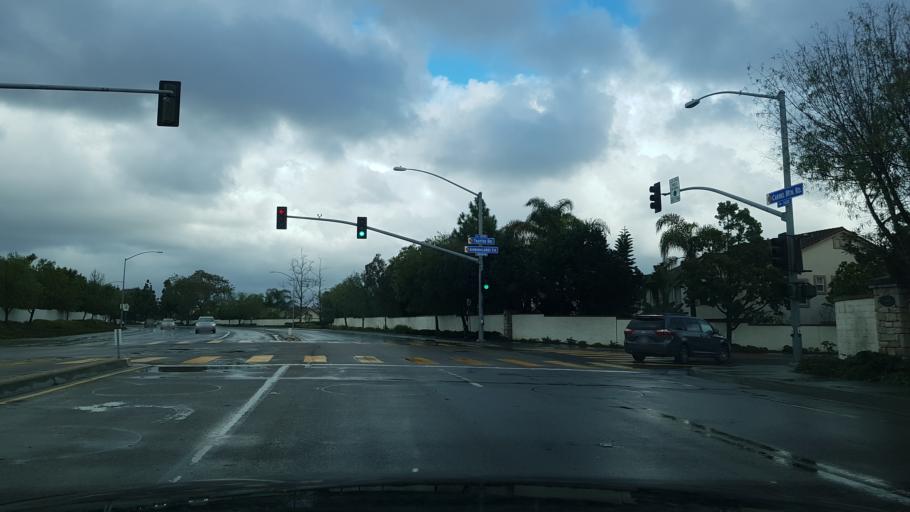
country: US
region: California
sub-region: San Diego County
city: Fairbanks Ranch
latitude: 32.9271
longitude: -117.2015
